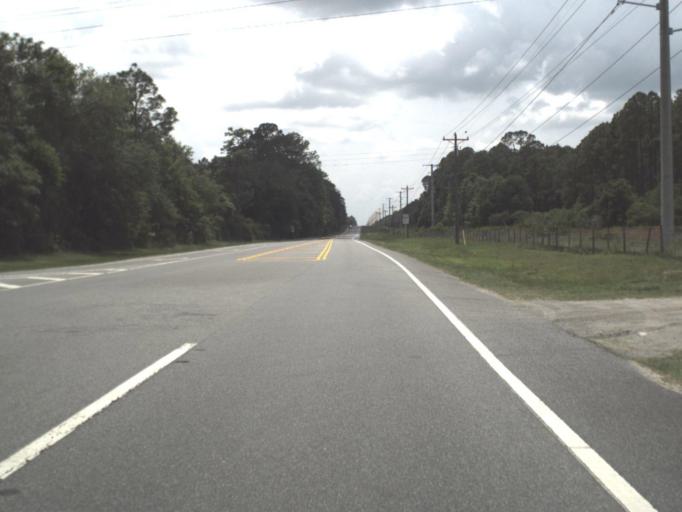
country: US
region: Florida
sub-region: Clay County
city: Keystone Heights
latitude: 29.8775
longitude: -81.9264
